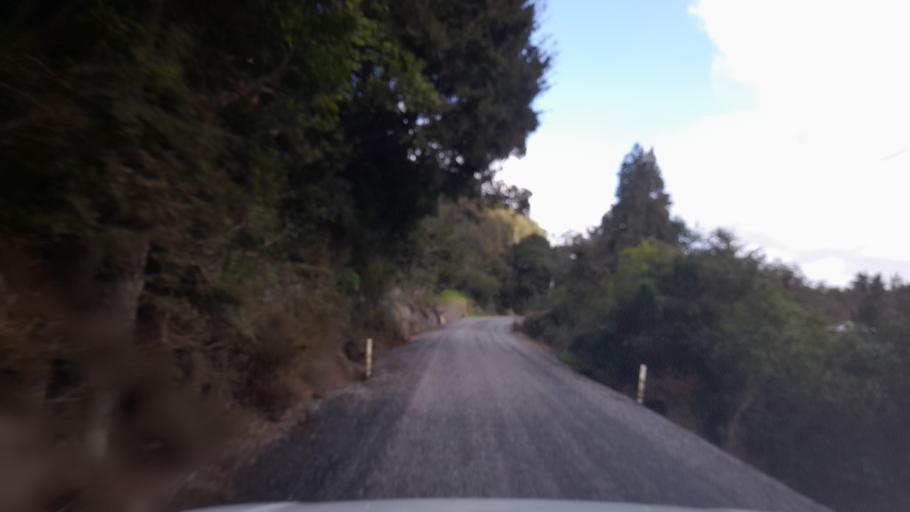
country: NZ
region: Northland
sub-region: Far North District
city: Kerikeri
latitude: -35.1321
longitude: 173.7334
